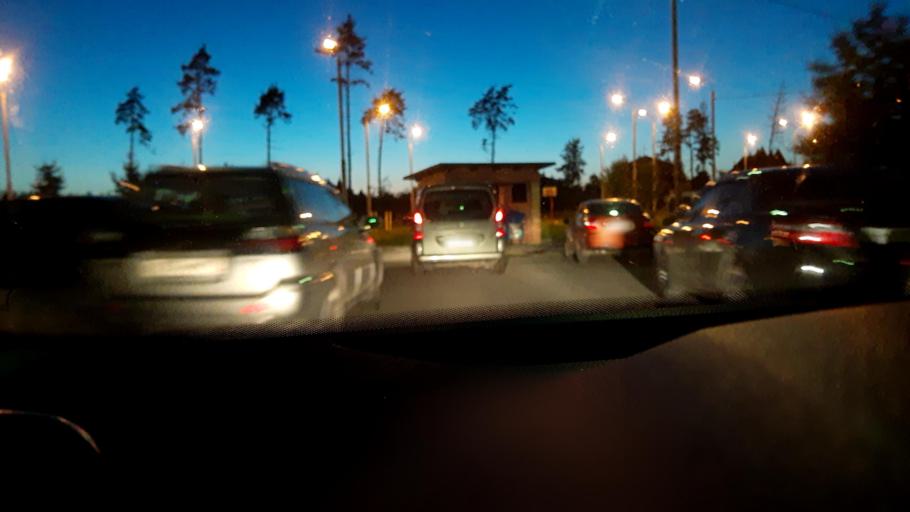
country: RU
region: Moskovskaya
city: Opalikha
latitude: 55.8340
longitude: 37.2375
